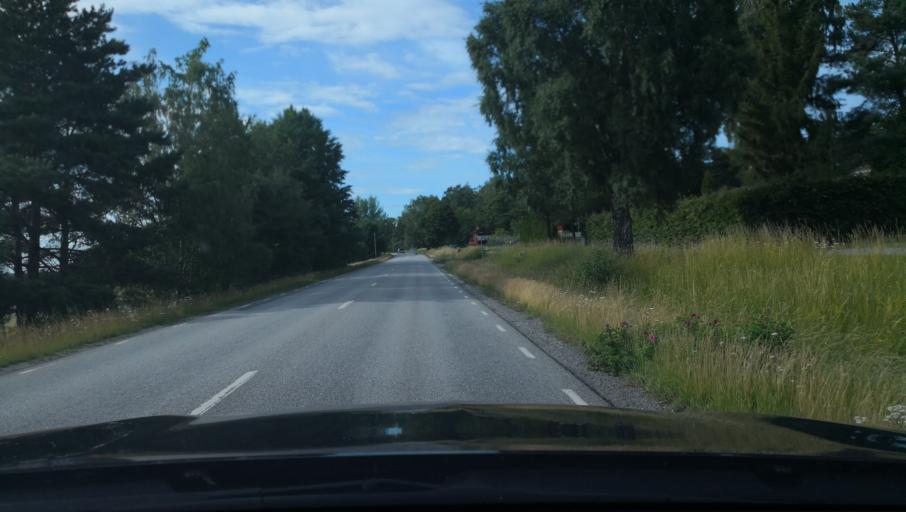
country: SE
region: Uppsala
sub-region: Habo Kommun
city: Balsta
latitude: 59.5978
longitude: 17.5094
